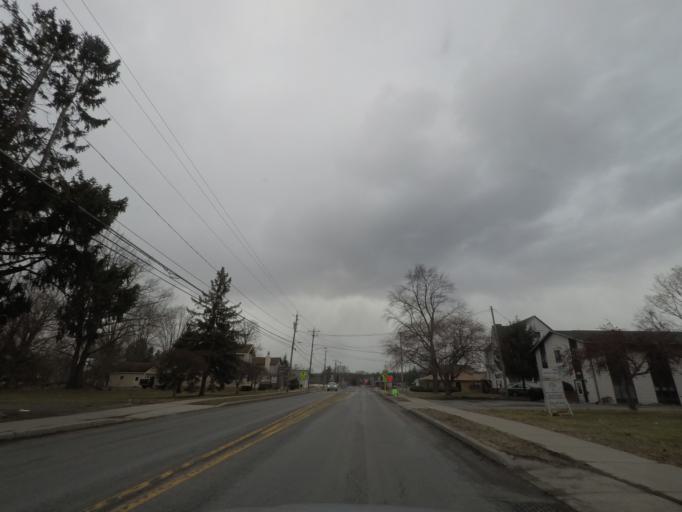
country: US
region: New York
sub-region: Madison County
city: Chittenango
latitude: 43.0516
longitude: -75.8659
